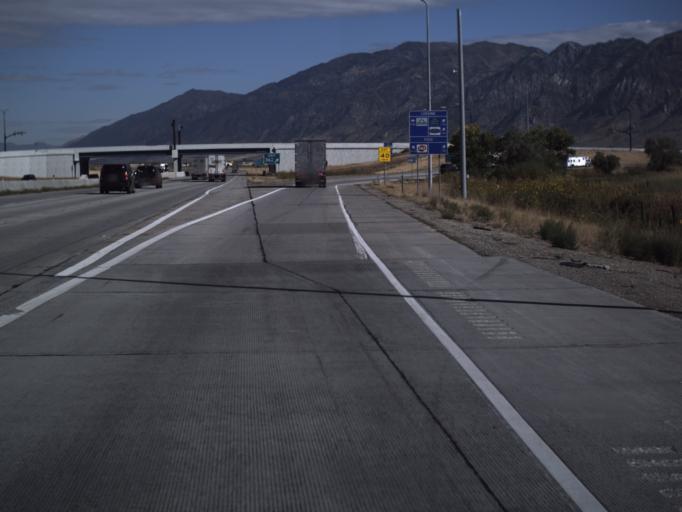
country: US
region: Utah
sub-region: Box Elder County
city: Perry
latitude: 41.4822
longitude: -112.0531
